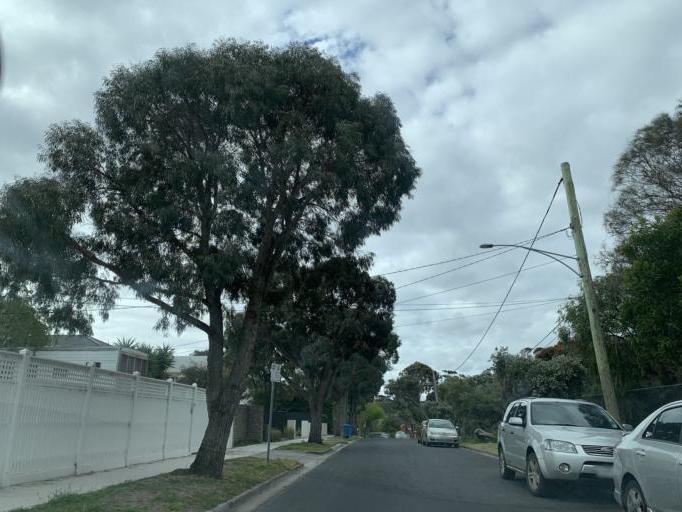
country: AU
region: Victoria
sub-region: Bayside
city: Black Rock
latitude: -37.9687
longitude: 145.0213
